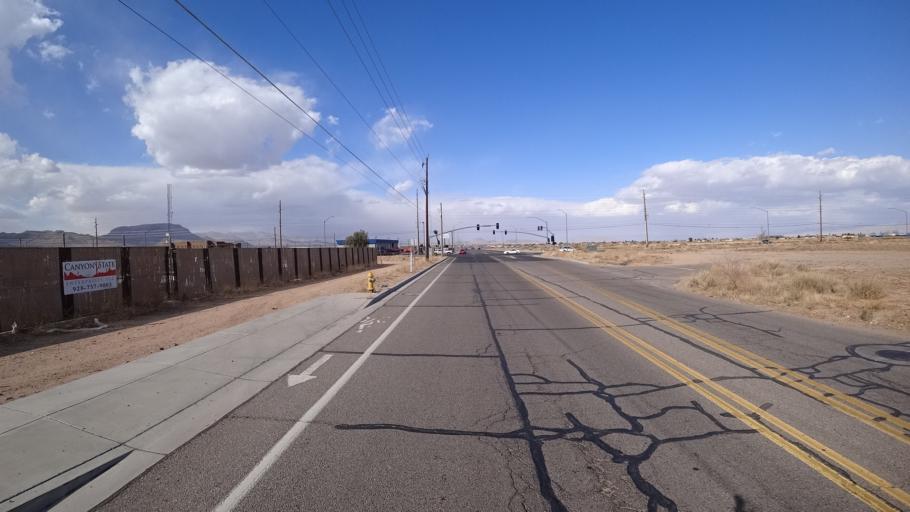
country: US
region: Arizona
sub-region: Mohave County
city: New Kingman-Butler
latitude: 35.2240
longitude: -114.0116
